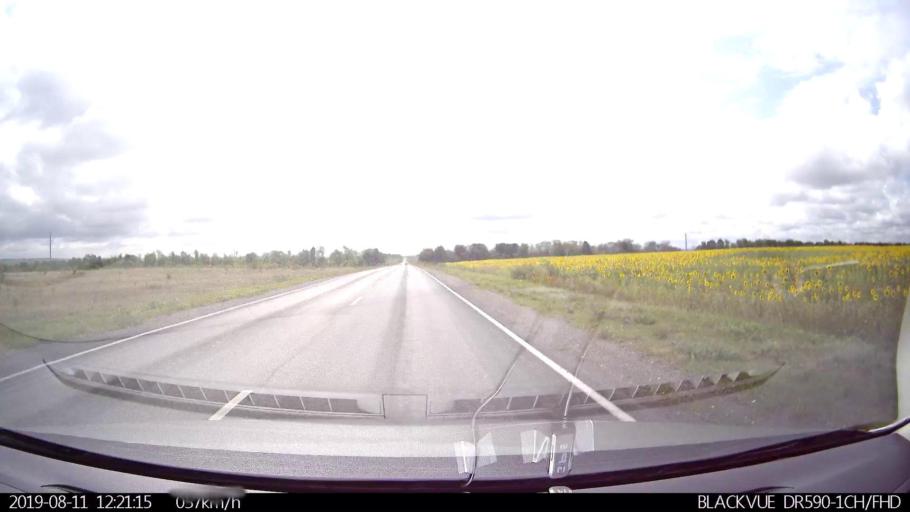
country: RU
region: Ulyanovsk
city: Ignatovka
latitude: 53.9226
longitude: 47.9580
